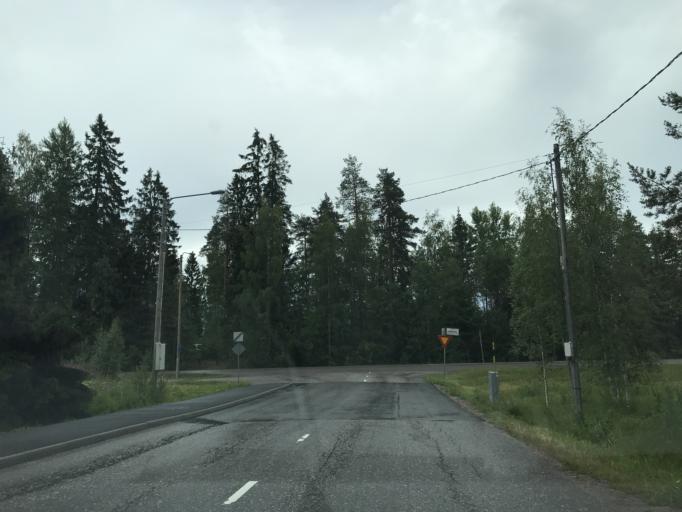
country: FI
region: Paijanne Tavastia
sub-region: Lahti
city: Orimattila
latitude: 60.8103
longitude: 25.7181
